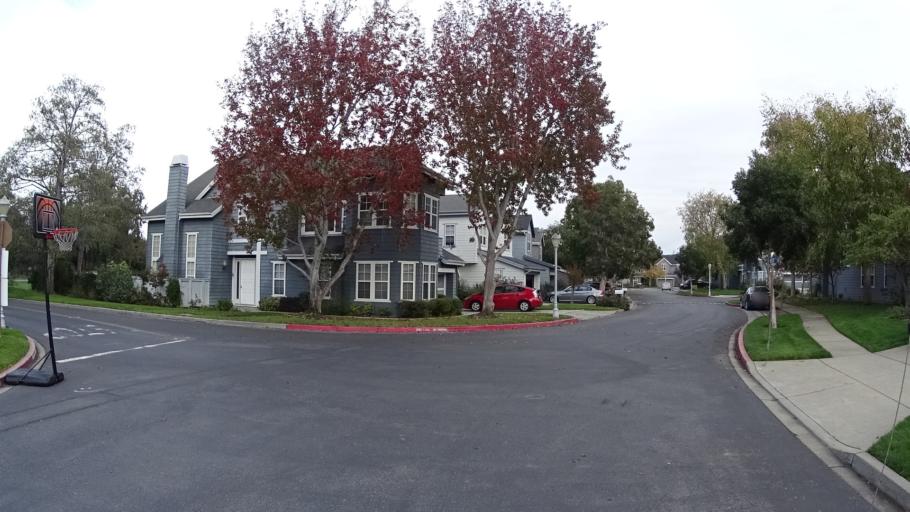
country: US
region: California
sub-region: San Mateo County
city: Redwood Shores
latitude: 37.5345
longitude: -122.2376
